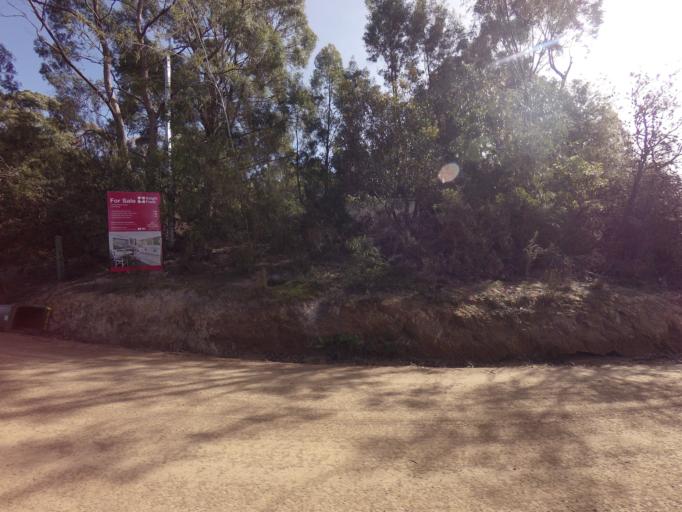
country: AU
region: Tasmania
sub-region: Kingborough
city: Margate
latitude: -43.0787
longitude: 147.2654
